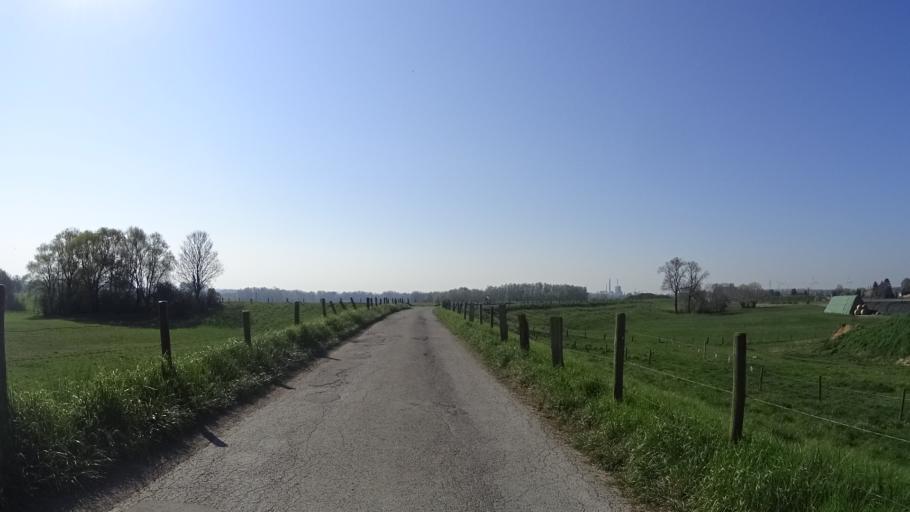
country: DE
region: North Rhine-Westphalia
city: Rheinberg
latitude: 51.5940
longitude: 6.5854
